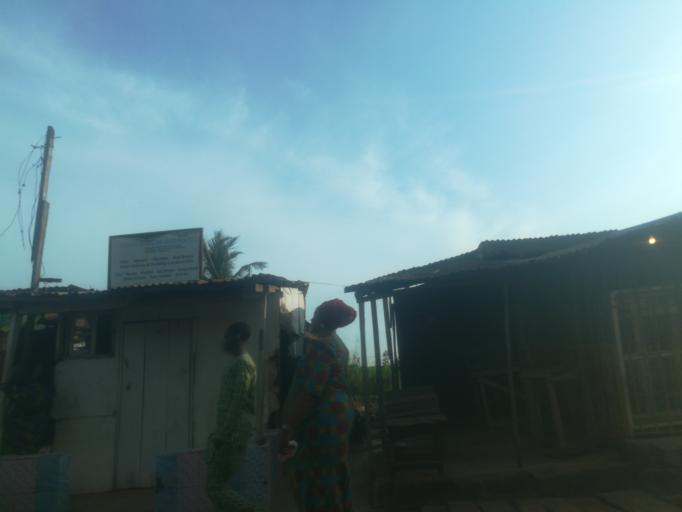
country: NG
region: Ogun
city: Abeokuta
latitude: 7.1180
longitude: 3.3240
